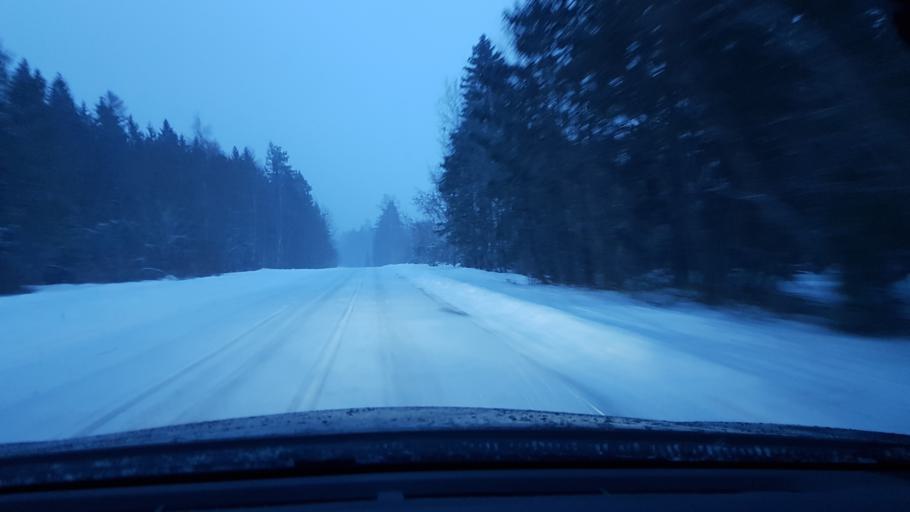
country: EE
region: Harju
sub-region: Loksa linn
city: Loksa
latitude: 59.4923
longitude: 25.6232
